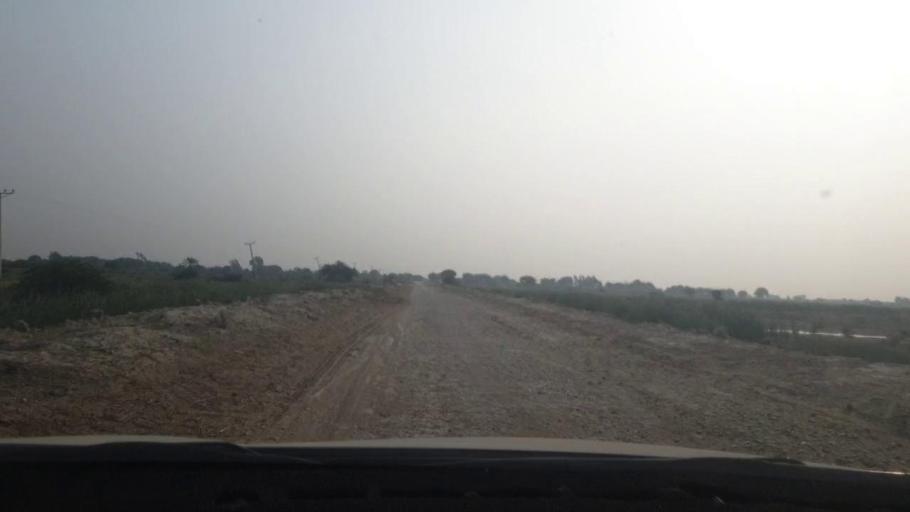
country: PK
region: Sindh
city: Bulri
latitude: 24.7931
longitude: 68.4269
